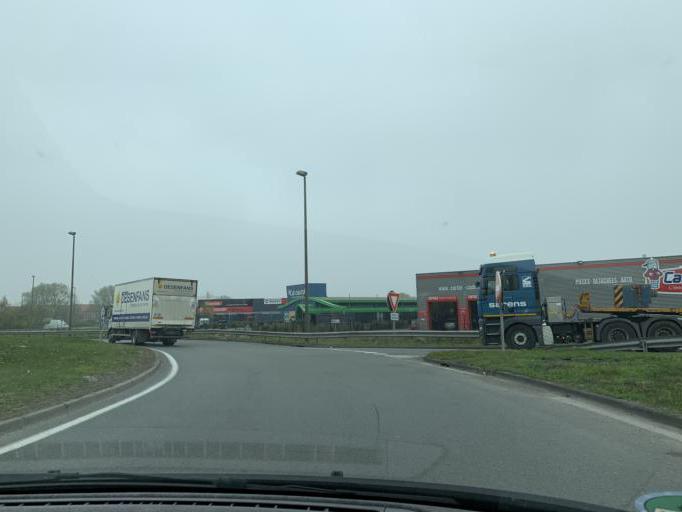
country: FR
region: Nord-Pas-de-Calais
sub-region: Departement du Nord
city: Cappelle-la-Grande
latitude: 51.0147
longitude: 2.3542
